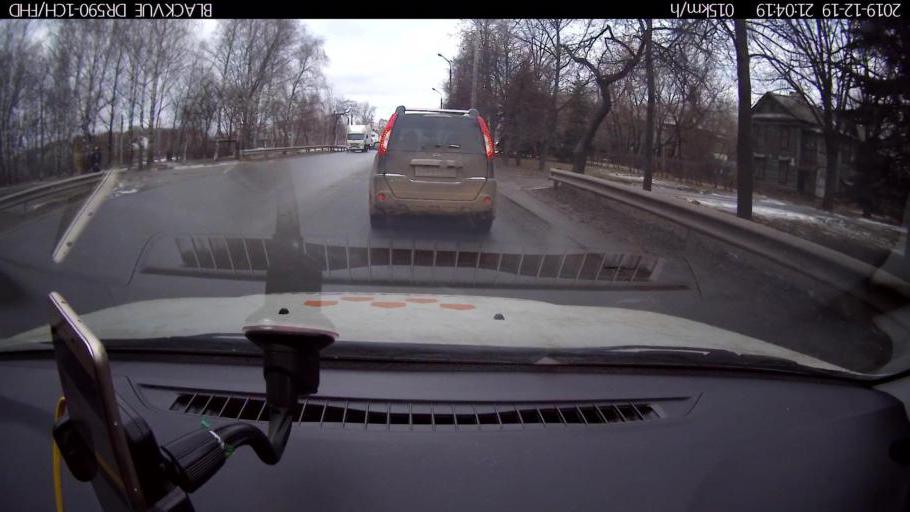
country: RU
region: Nizjnij Novgorod
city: Gorbatovka
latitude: 56.3463
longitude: 43.8389
